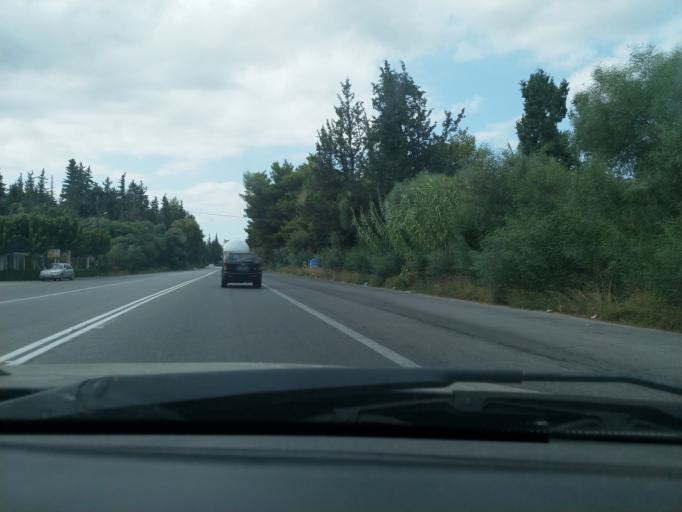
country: GR
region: Crete
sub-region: Nomos Chanias
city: Georgioupolis
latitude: 35.3652
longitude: 24.2193
